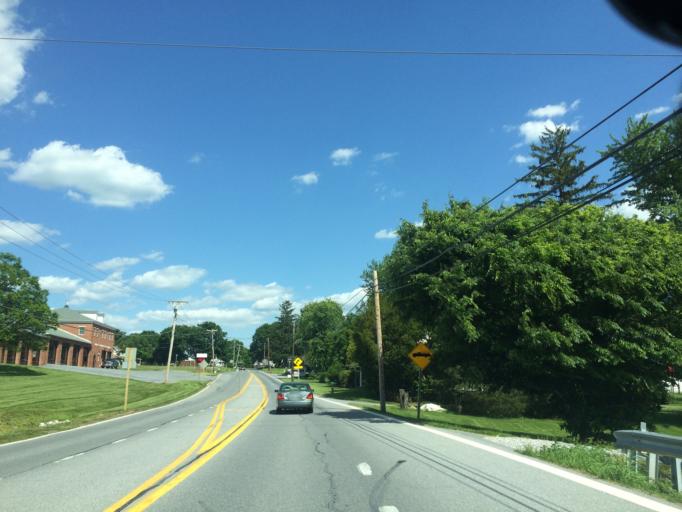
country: US
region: Maryland
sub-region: Carroll County
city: Eldersburg
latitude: 39.4684
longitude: -76.9412
